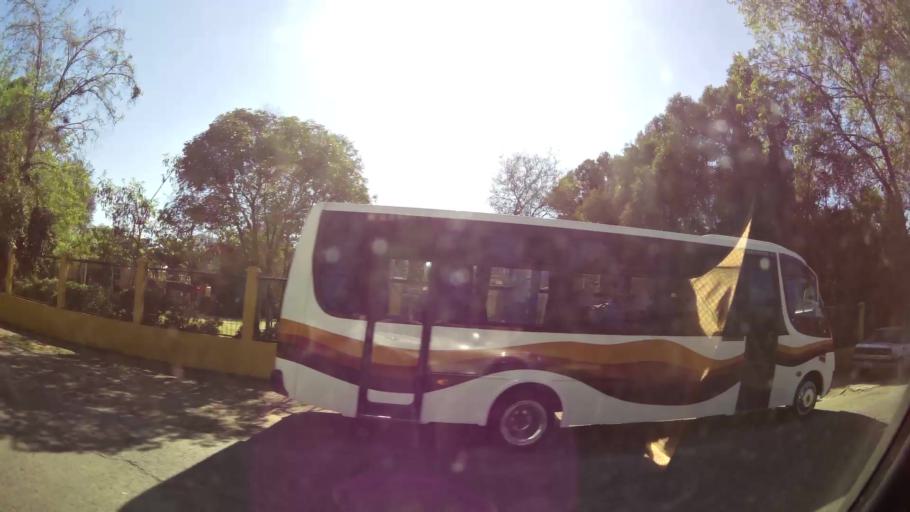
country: CL
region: Santiago Metropolitan
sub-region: Provincia de Talagante
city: Penaflor
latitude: -33.6024
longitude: -70.8972
